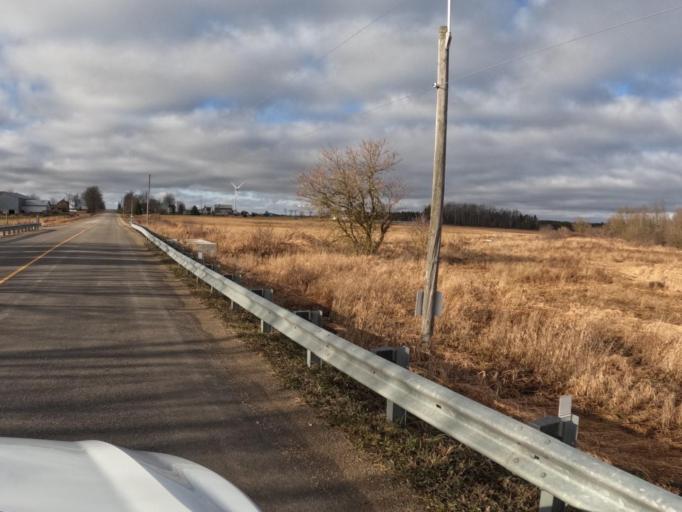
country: CA
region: Ontario
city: Shelburne
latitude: 43.8923
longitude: -80.3478
